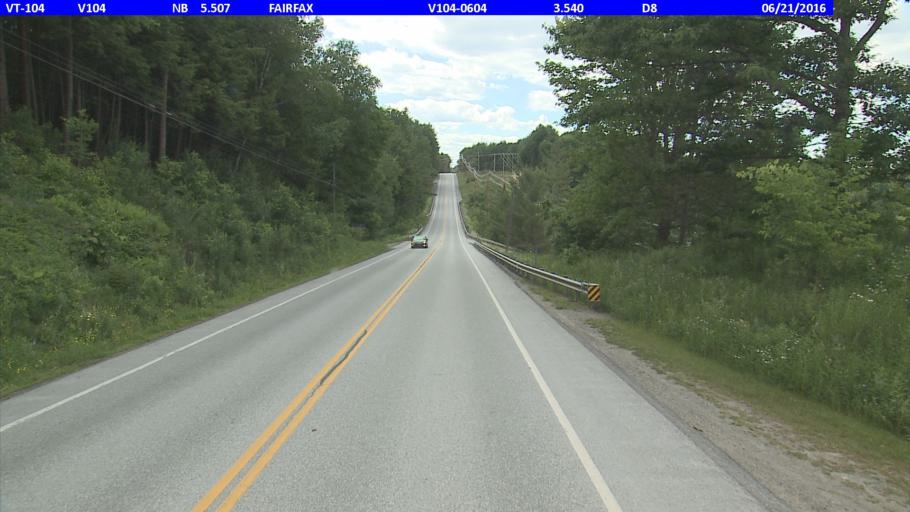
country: US
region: Vermont
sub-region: Chittenden County
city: Milton
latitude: 44.6508
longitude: -72.9908
